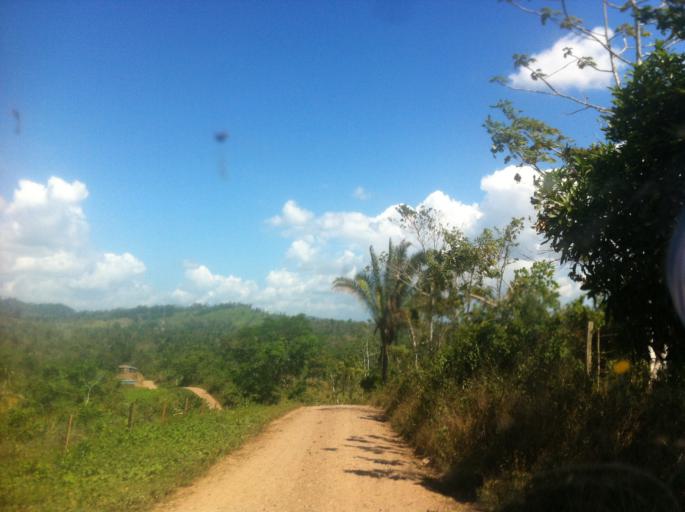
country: CR
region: Alajuela
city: Los Chiles
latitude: 11.2490
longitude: -84.4510
